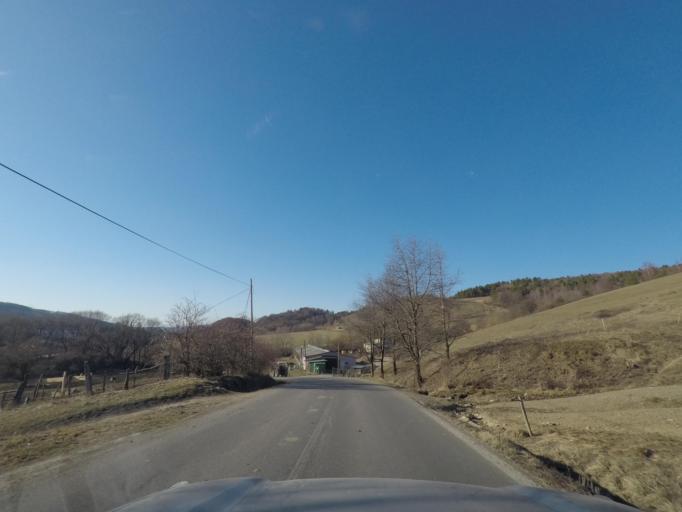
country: SK
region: Presovsky
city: Medzilaborce
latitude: 49.2194
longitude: 21.9803
